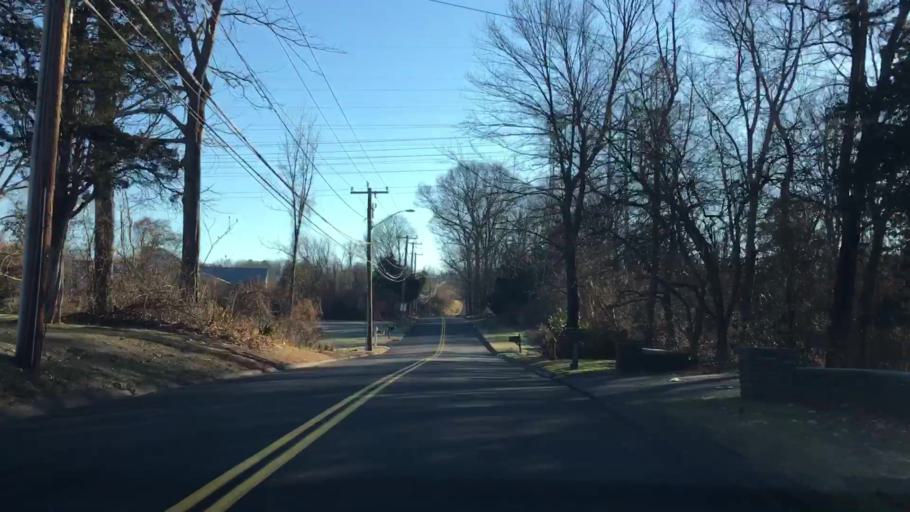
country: US
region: Connecticut
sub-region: New Haven County
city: Meriden
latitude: 41.5476
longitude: -72.8597
